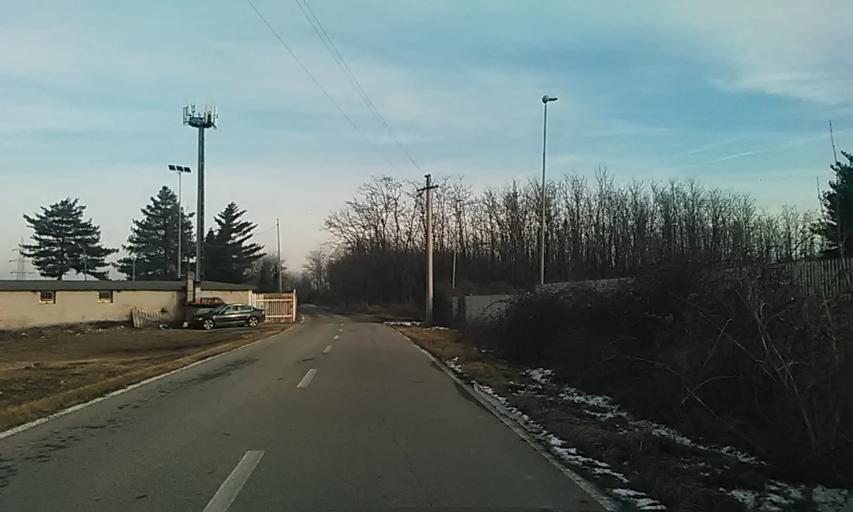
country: IT
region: Piedmont
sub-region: Provincia di Novara
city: Recetto
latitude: 45.4660
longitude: 8.4264
